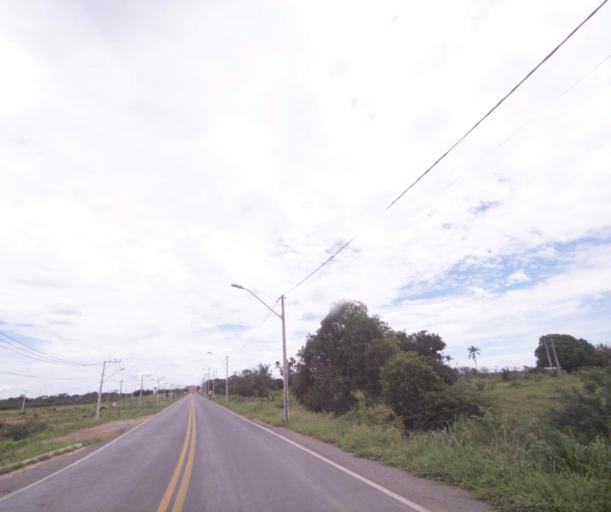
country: BR
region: Bahia
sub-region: Carinhanha
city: Carinhanha
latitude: -14.3296
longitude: -43.7674
